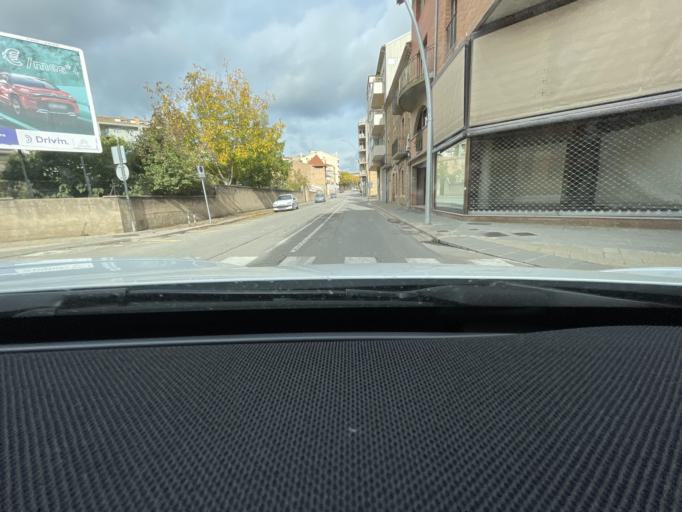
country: ES
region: Catalonia
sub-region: Provincia de Lleida
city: Solsona
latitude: 41.9926
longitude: 1.5134
